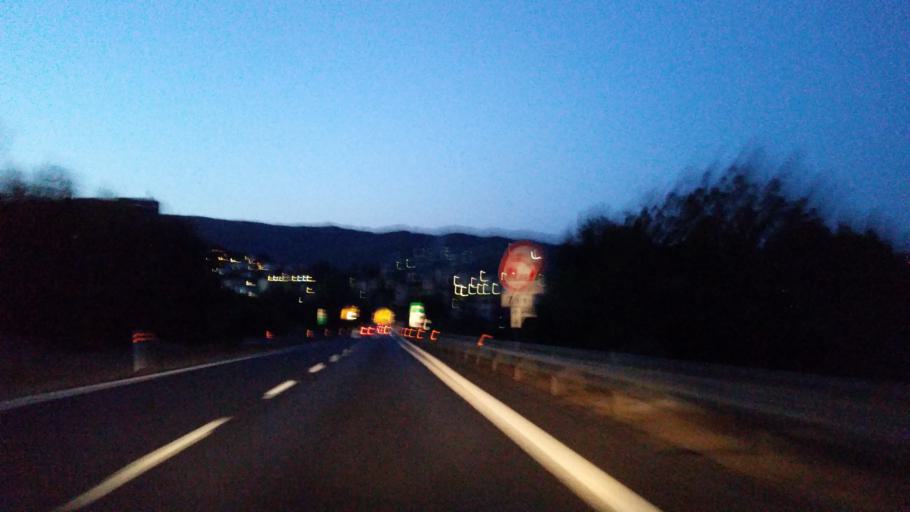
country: IT
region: Liguria
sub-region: Provincia di Imperia
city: Diano Castello
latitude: 43.9131
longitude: 8.0689
